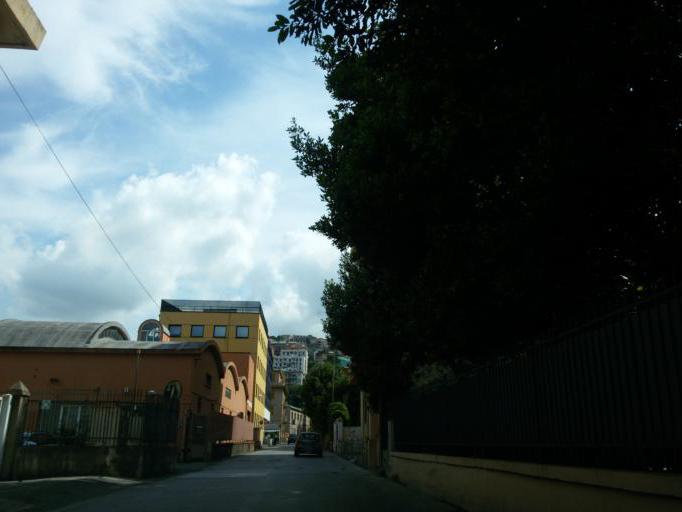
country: IT
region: Liguria
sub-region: Provincia di Genova
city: Genoa
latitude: 44.3971
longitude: 8.9859
